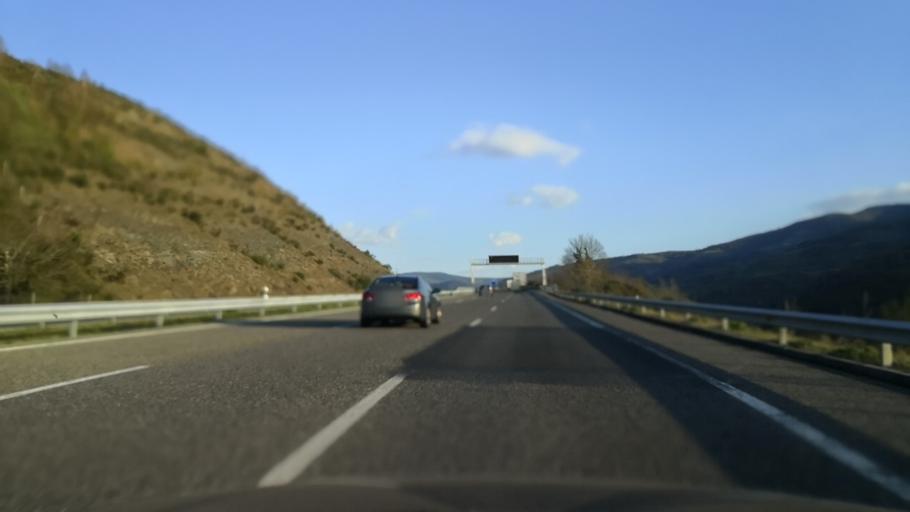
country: ES
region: Galicia
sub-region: Provincia de Lugo
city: San Roman
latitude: 42.7766
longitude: -7.0975
